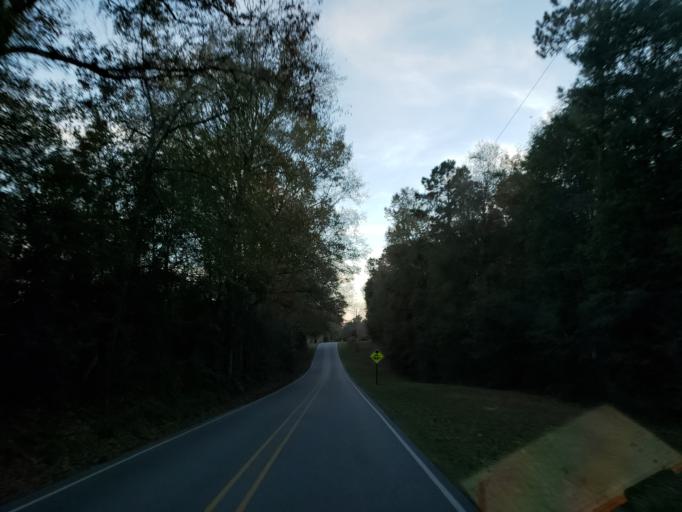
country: US
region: Mississippi
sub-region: Forrest County
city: Hattiesburg
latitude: 31.2463
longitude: -89.3140
